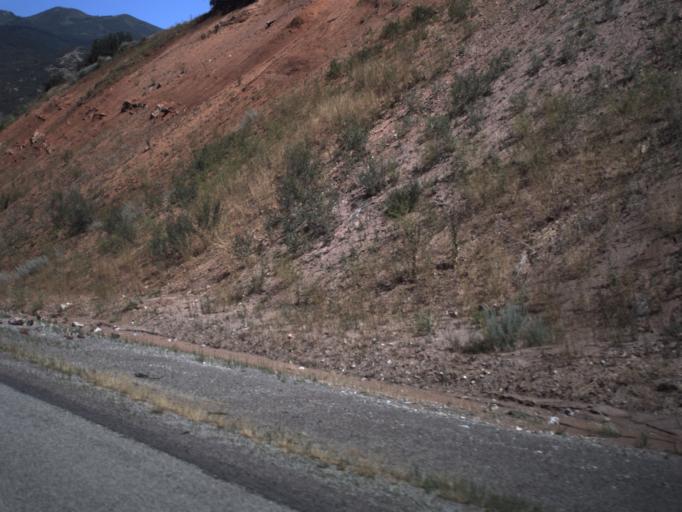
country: US
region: Utah
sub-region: Utah County
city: Mapleton
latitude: 40.0216
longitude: -111.4981
